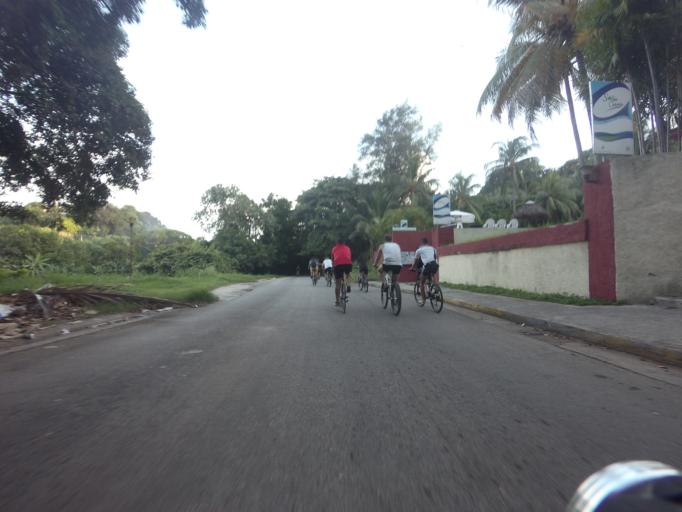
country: CU
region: La Habana
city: Havana
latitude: 23.1157
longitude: -82.4069
